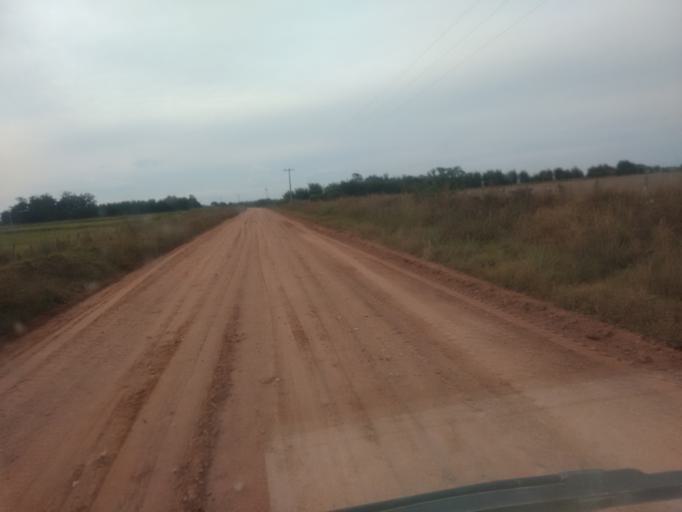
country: BR
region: Rio Grande do Sul
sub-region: Camaqua
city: Camaqua
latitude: -31.1432
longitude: -51.7626
